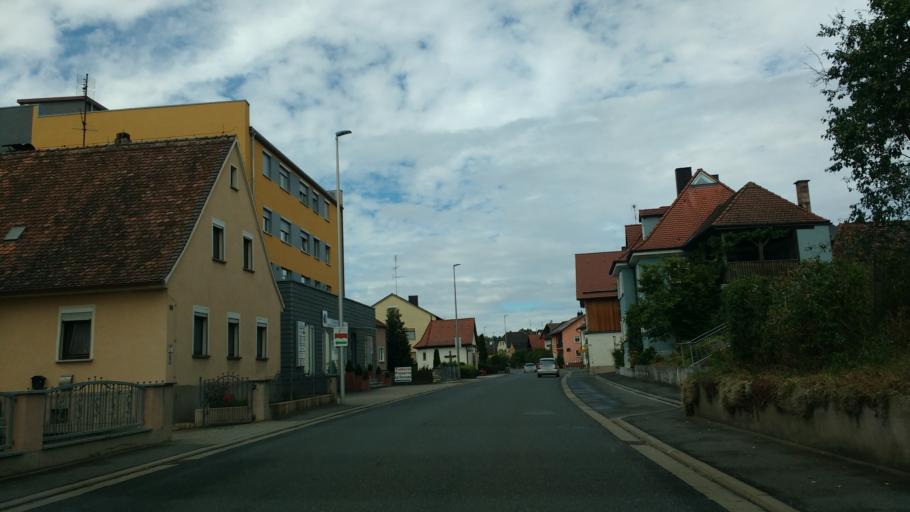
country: DE
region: Bavaria
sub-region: Upper Franconia
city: Schlusselfeld
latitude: 49.7515
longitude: 10.6281
